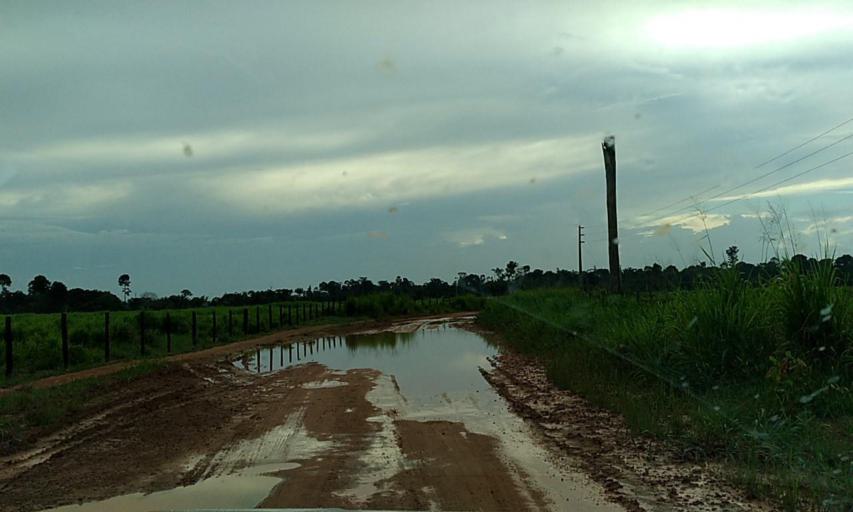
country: BR
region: Para
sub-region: Senador Jose Porfirio
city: Senador Jose Porfirio
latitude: -2.5598
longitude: -51.8811
